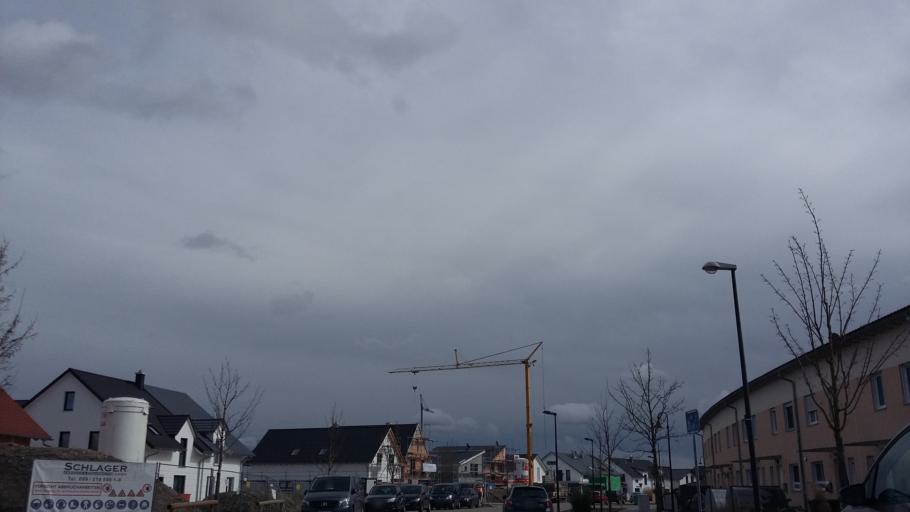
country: DE
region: Bavaria
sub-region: Upper Bavaria
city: Grobenzell
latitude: 48.2178
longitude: 11.3501
